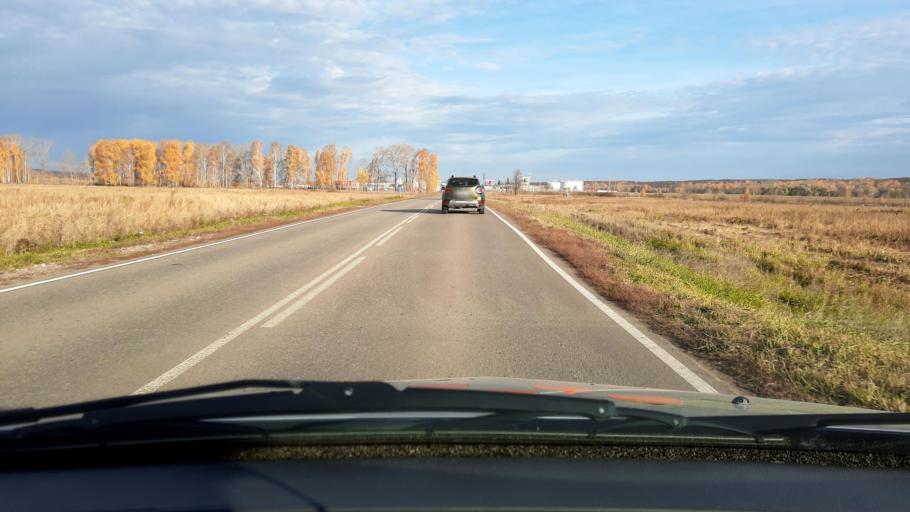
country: RU
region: Bashkortostan
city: Mikhaylovka
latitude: 54.8186
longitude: 55.7671
